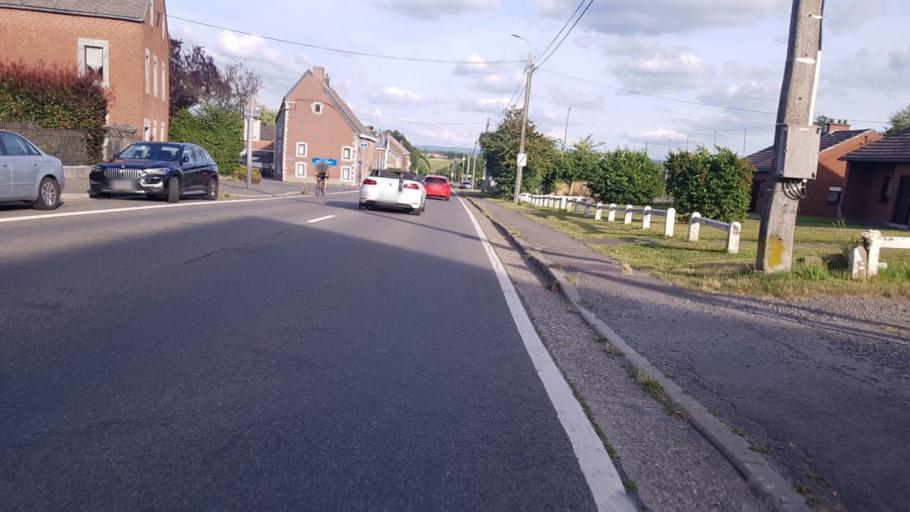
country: BE
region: Wallonia
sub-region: Province de Liege
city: Soumagne
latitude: 50.6083
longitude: 5.7146
